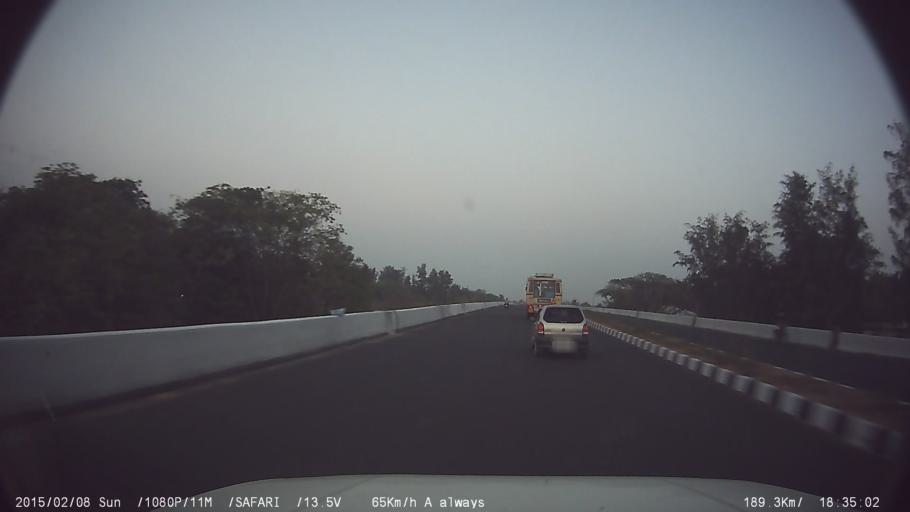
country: IN
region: Kerala
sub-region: Palakkad district
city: Palakkad
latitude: 10.7920
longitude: 76.7258
